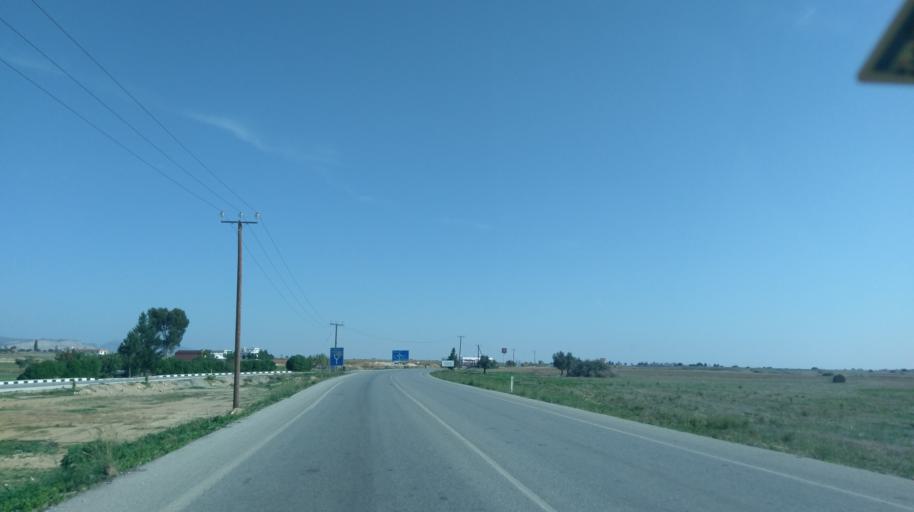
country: CY
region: Ammochostos
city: Lefkonoiko
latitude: 35.2604
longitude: 33.7421
